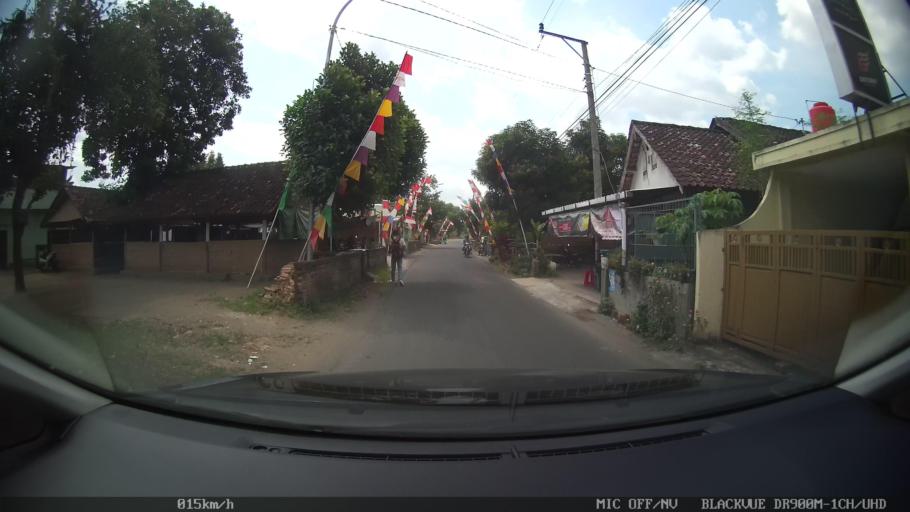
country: ID
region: Daerah Istimewa Yogyakarta
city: Kasihan
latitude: -7.8155
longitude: 110.3403
